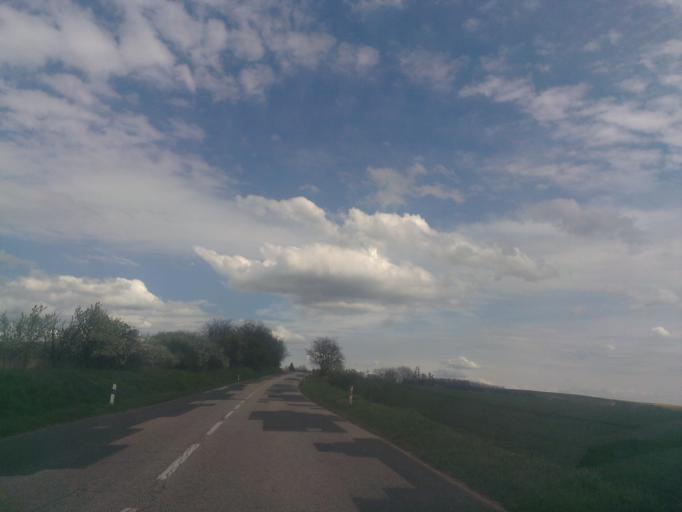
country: CZ
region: South Moravian
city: Orechov
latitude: 49.1092
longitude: 16.5022
